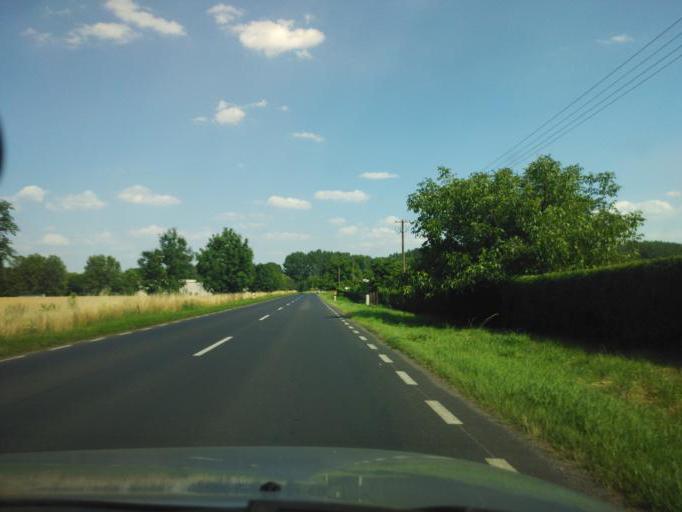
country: PL
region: West Pomeranian Voivodeship
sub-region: Powiat pyrzycki
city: Pyrzyce
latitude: 53.1364
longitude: 14.9151
